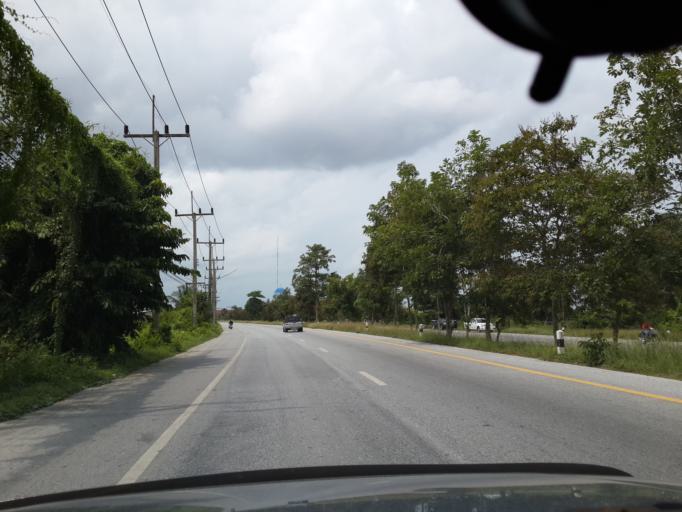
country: TH
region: Pattani
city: Yaring
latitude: 6.8689
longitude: 101.3553
